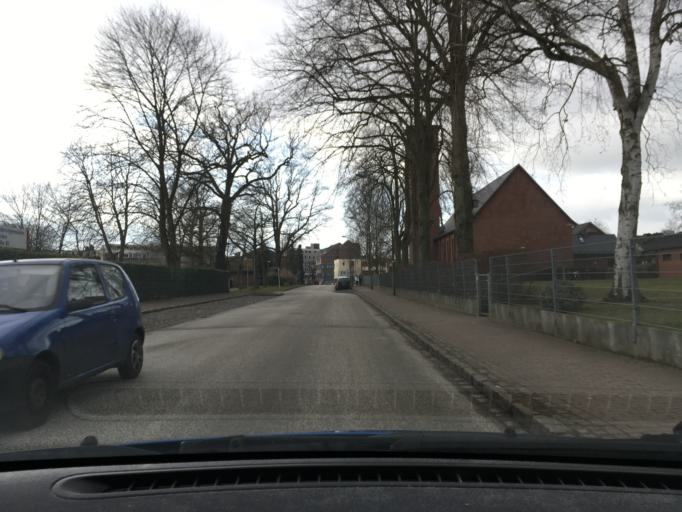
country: DE
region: Schleswig-Holstein
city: Wedel
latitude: 53.5768
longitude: 9.7092
